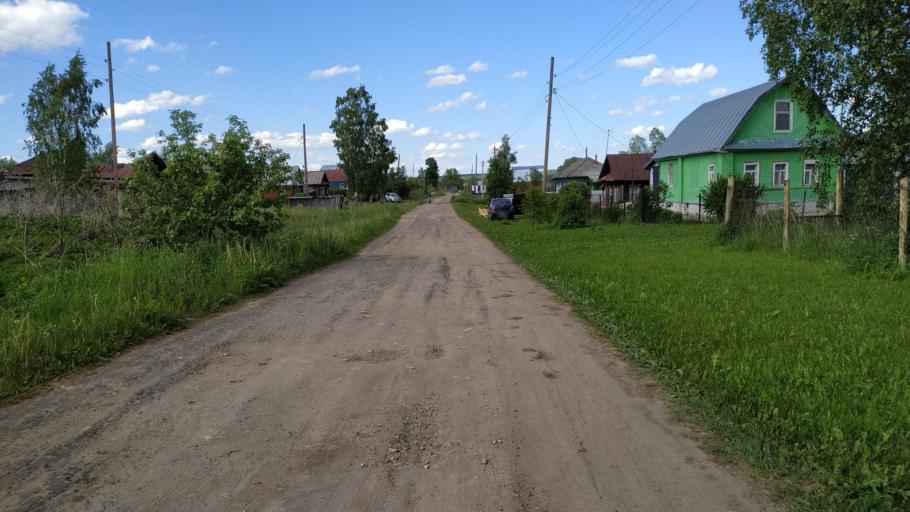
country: RU
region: Nizjnij Novgorod
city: Bogorodsk
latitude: 55.8840
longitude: 43.5566
